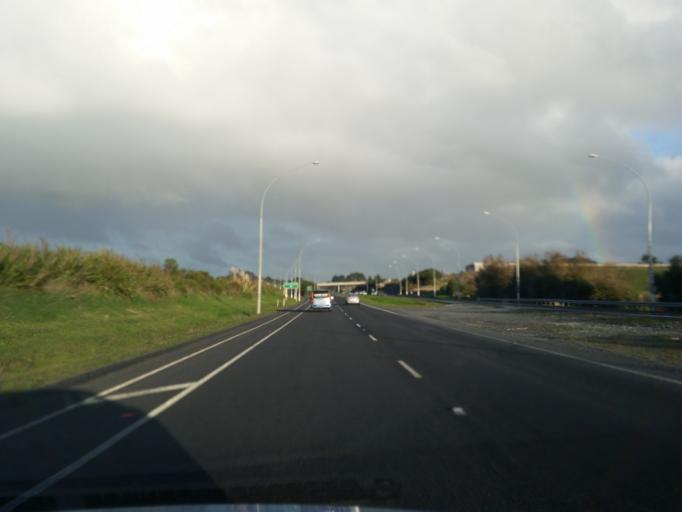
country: NZ
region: Waikato
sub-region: Waikato District
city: Te Kauwhata
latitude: -37.3509
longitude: 175.0795
